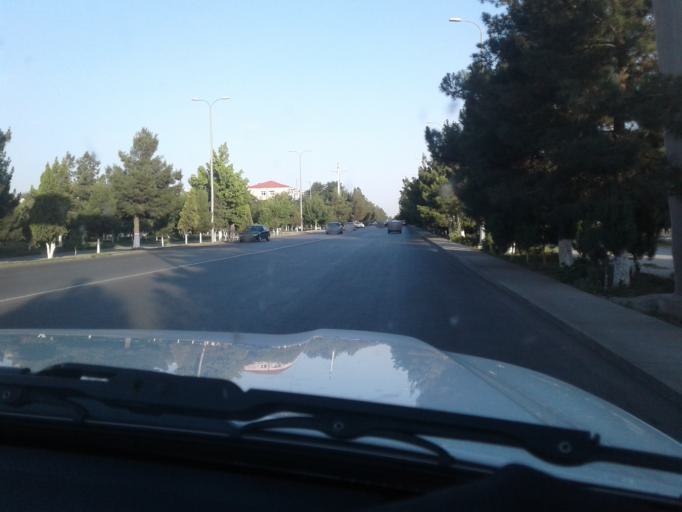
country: TM
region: Mary
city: Mary
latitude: 37.5841
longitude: 61.8599
